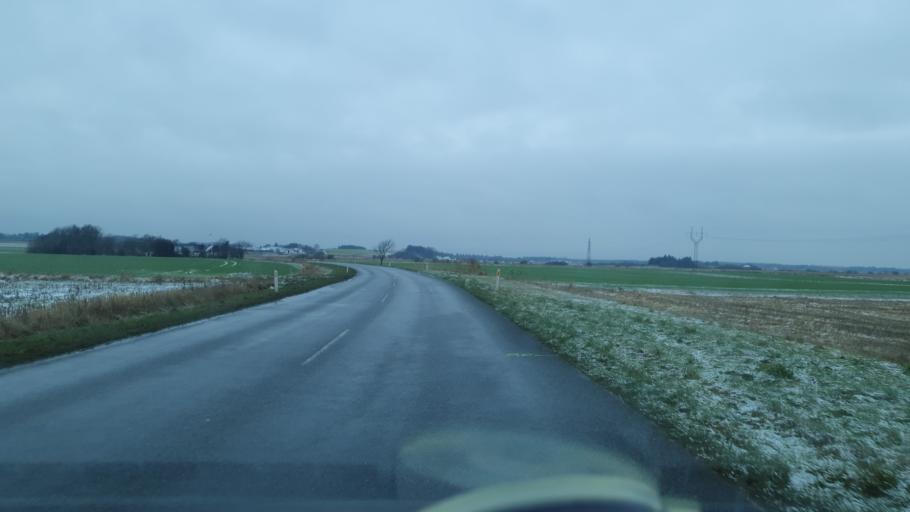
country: DK
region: North Denmark
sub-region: Jammerbugt Kommune
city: Brovst
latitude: 57.1156
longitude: 9.5003
